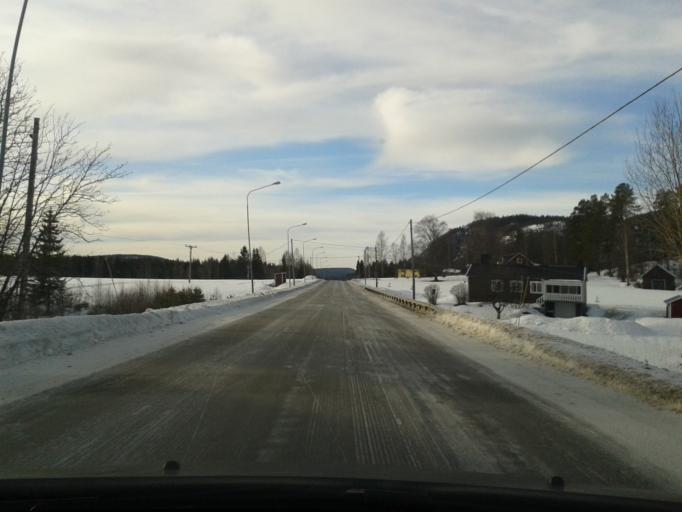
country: SE
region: Vaesternorrland
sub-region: OErnskoeldsviks Kommun
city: Bredbyn
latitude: 63.5264
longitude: 18.0315
